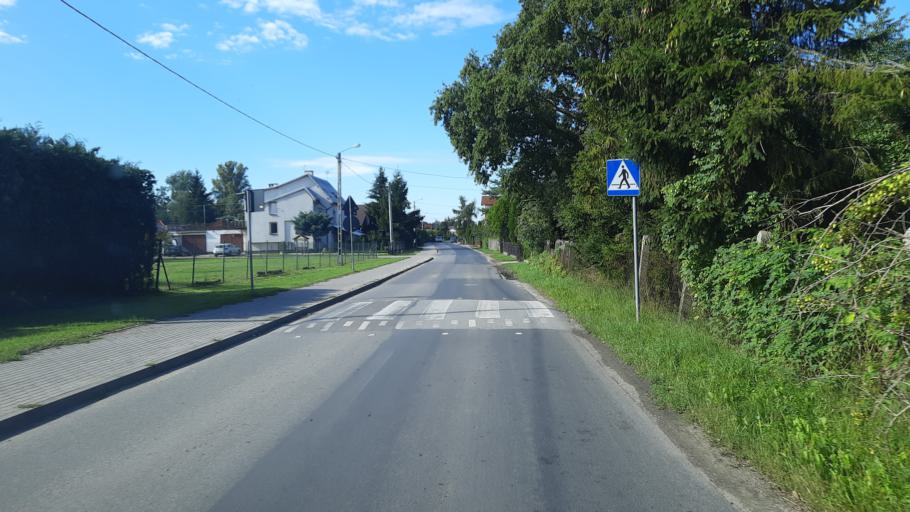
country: PL
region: Lower Silesian Voivodeship
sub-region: Powiat wroclawski
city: Dlugoleka
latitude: 51.1945
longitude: 17.1823
